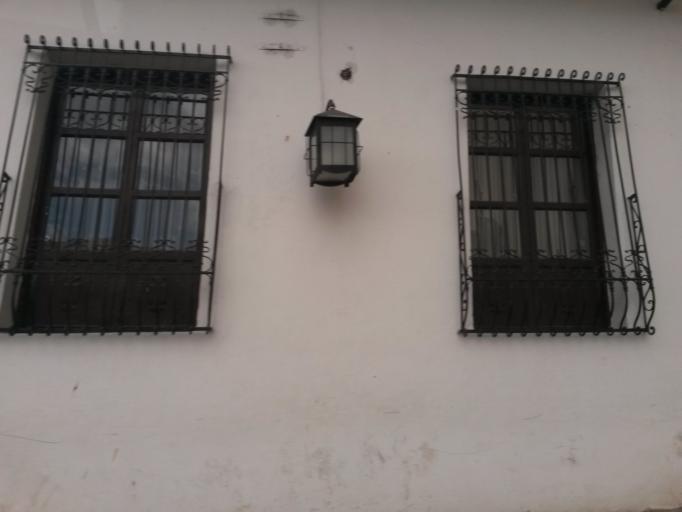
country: CO
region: Cauca
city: Popayan
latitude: 2.4425
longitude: -76.6034
